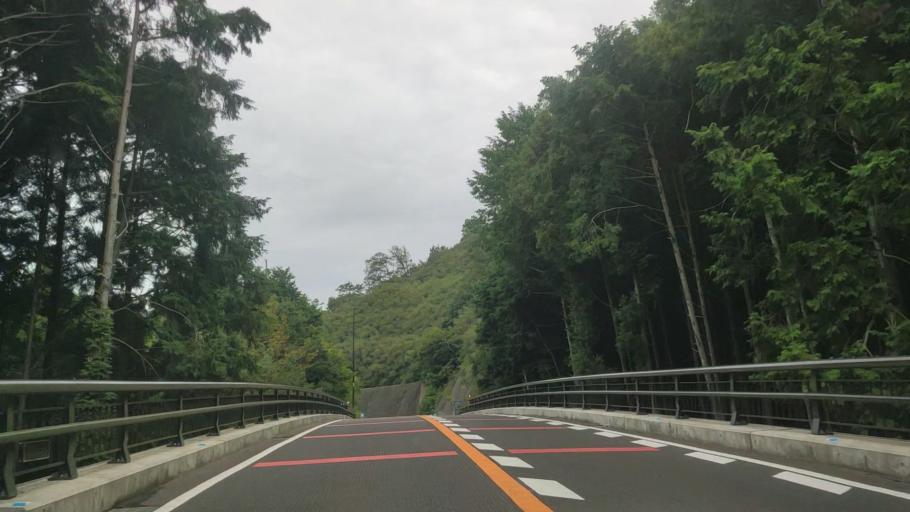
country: JP
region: Wakayama
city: Hashimoto
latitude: 34.3979
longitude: 135.5974
